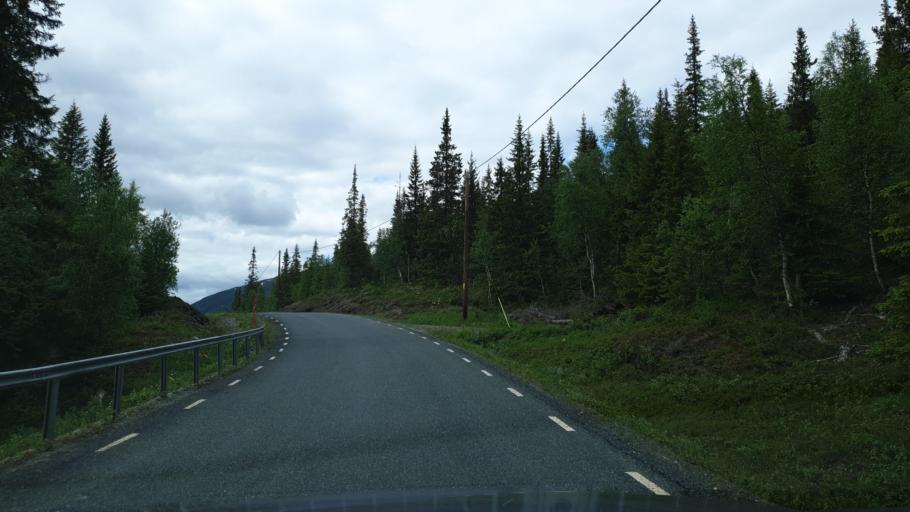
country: NO
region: Nordland
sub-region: Hattfjelldal
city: Hattfjelldal
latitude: 65.4296
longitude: 14.5957
